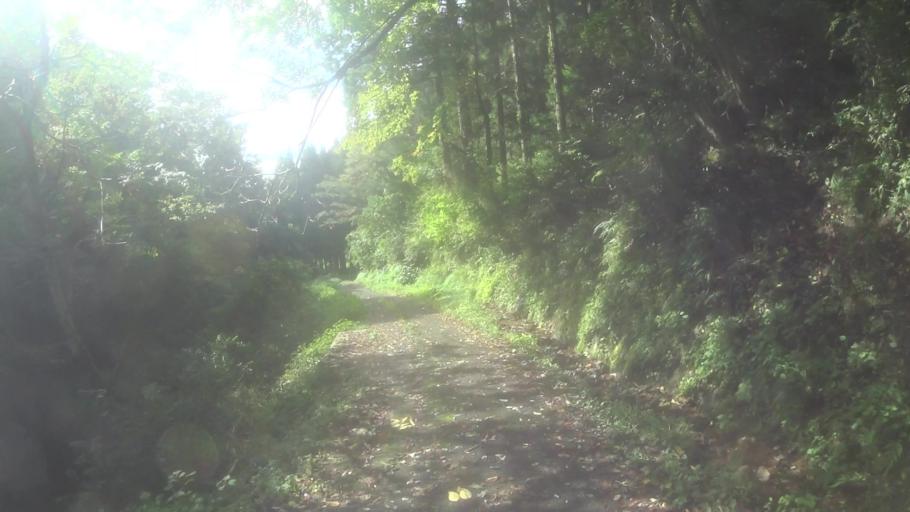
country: JP
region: Kyoto
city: Miyazu
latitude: 35.6231
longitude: 135.1562
